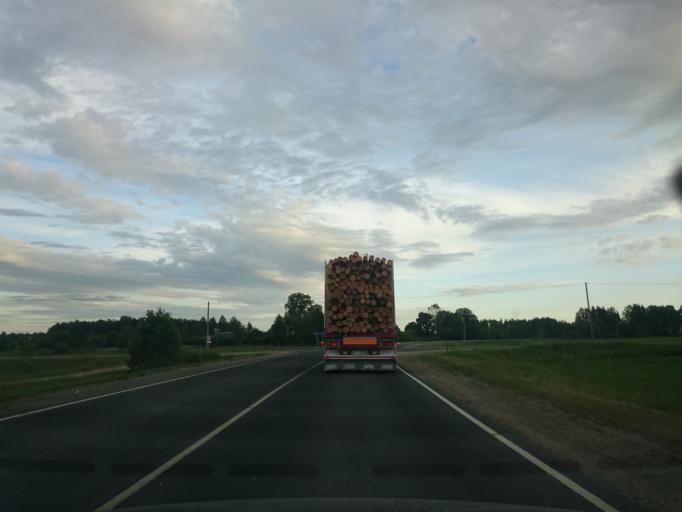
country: LV
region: Incukalns
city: Incukalns
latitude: 57.0958
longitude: 24.7017
